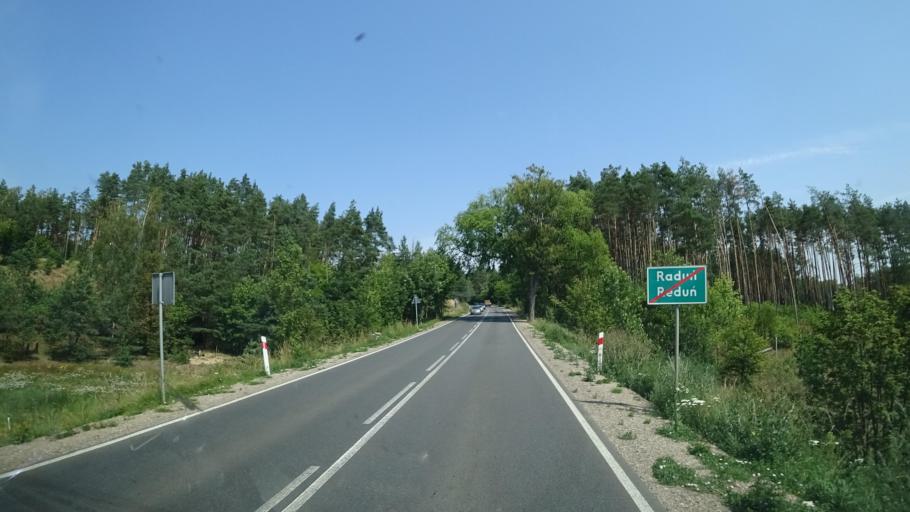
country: PL
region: Pomeranian Voivodeship
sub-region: Powiat koscierski
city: Dziemiany
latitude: 53.9759
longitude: 17.7696
